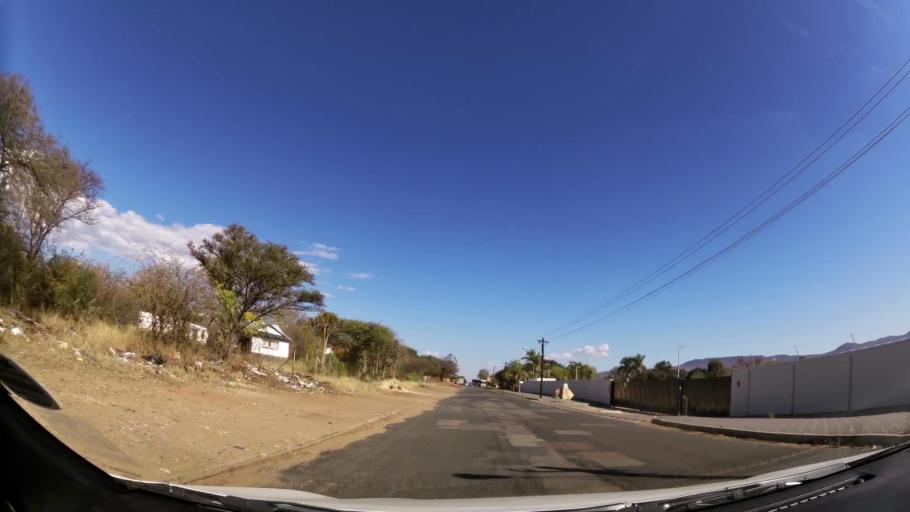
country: ZA
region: Limpopo
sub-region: Waterberg District Municipality
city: Mokopane
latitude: -24.1771
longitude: 29.0175
